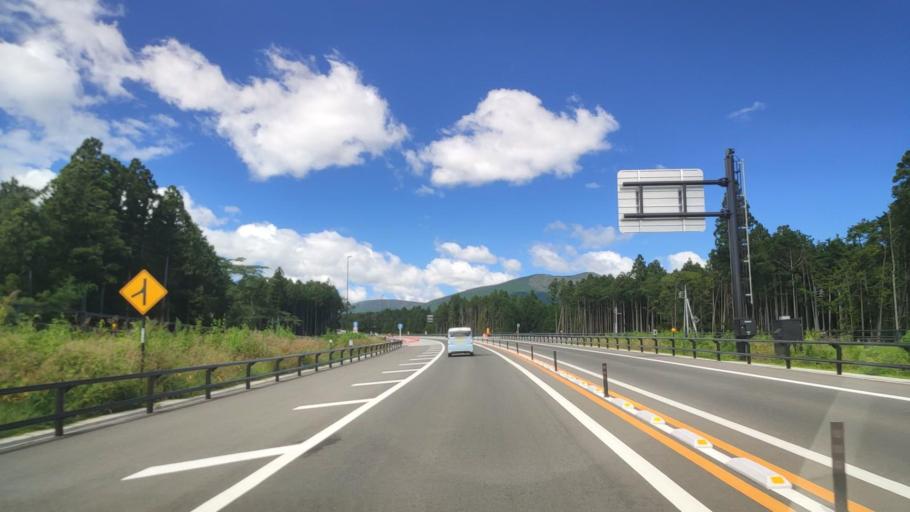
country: JP
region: Shizuoka
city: Gotemba
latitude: 35.3279
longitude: 138.9022
